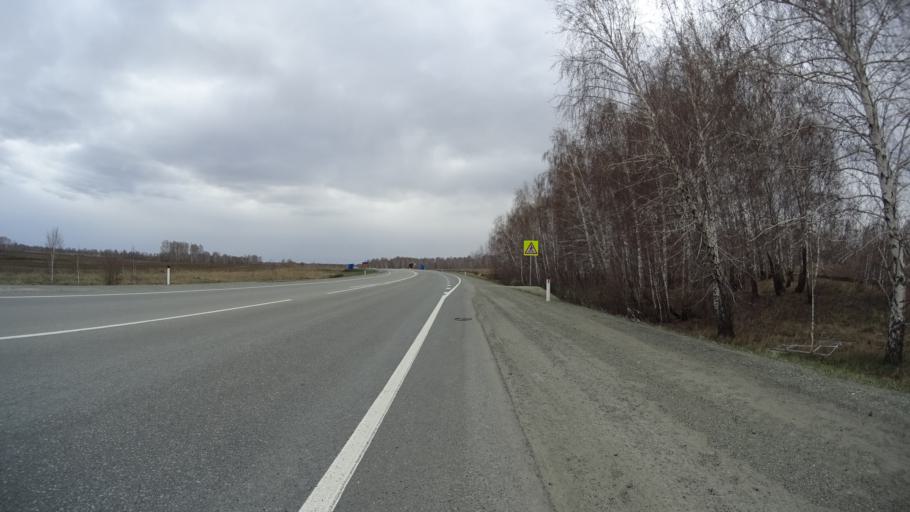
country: RU
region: Chelyabinsk
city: Yemanzhelinsk
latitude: 54.6981
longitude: 61.2507
